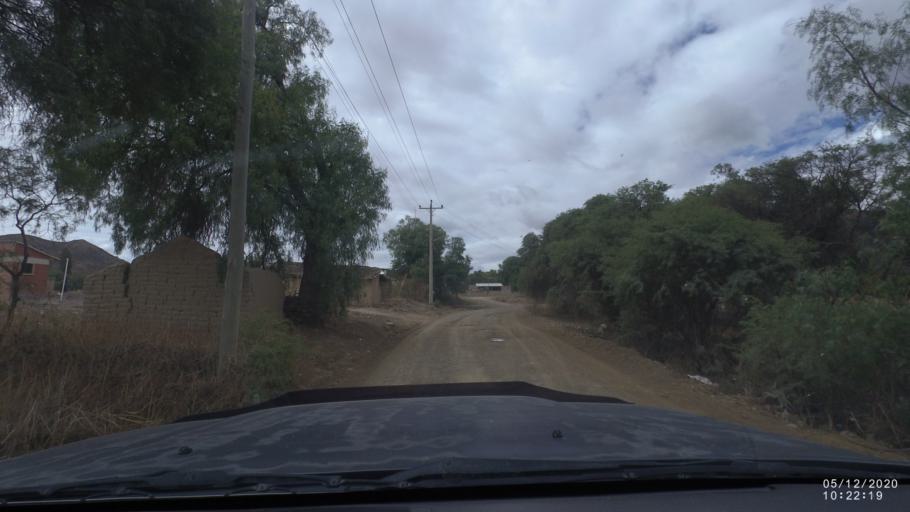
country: BO
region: Cochabamba
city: Sipe Sipe
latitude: -17.4953
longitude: -66.2821
